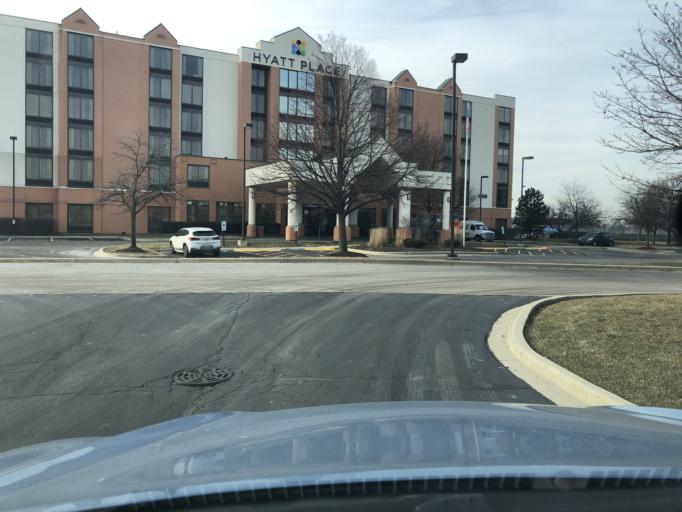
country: US
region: Illinois
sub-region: DuPage County
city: Itasca
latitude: 41.9869
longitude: -88.0041
